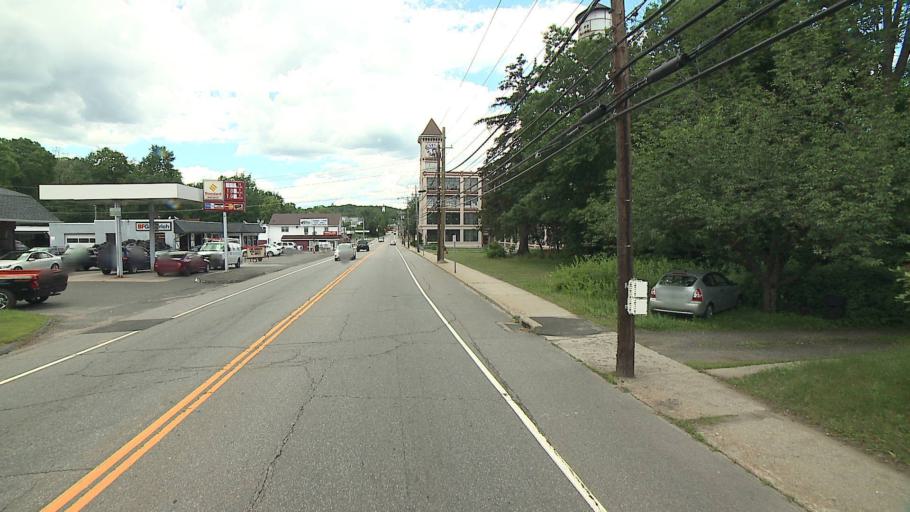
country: US
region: Connecticut
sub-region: Litchfield County
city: Thomaston
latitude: 41.6686
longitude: -73.0783
